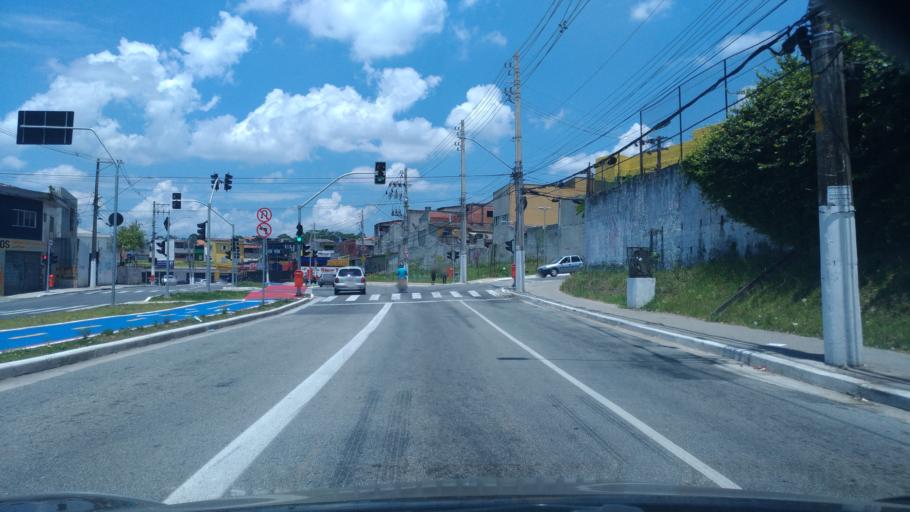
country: BR
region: Sao Paulo
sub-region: Sao Bernardo Do Campo
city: Sao Bernardo do Campo
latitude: -23.7358
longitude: -46.5895
